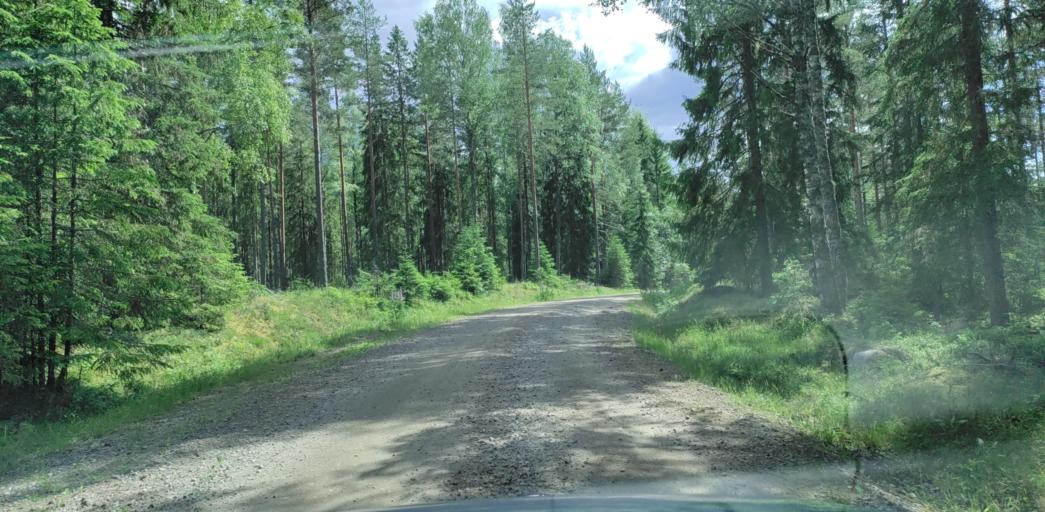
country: SE
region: Vaermland
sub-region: Hagfors Kommun
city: Ekshaerad
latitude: 60.0588
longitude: 13.3108
